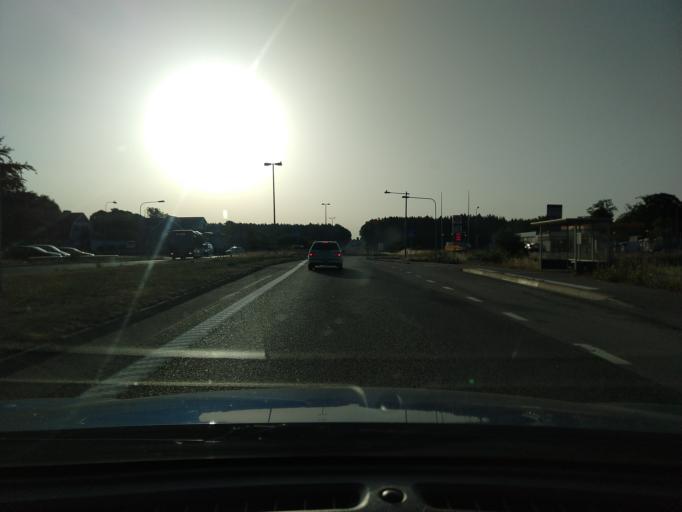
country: SE
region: Blekinge
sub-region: Karlskrona Kommun
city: Nattraby
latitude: 56.1995
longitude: 15.4019
